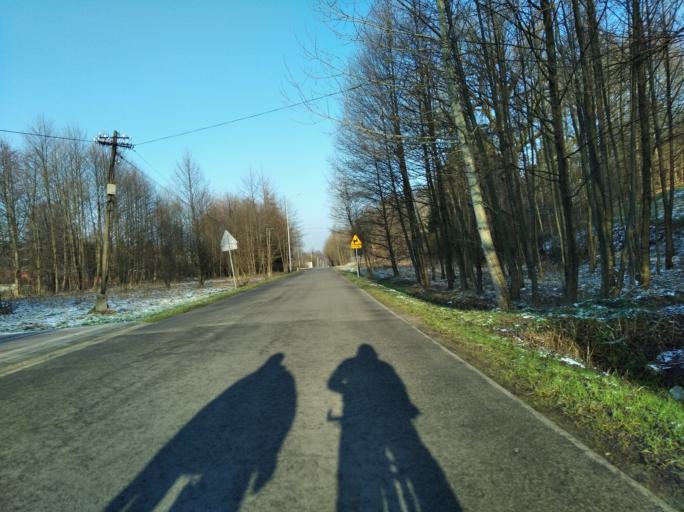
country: PL
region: Subcarpathian Voivodeship
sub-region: Powiat strzyzowski
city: Konieczkowa
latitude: 49.8322
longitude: 21.9330
